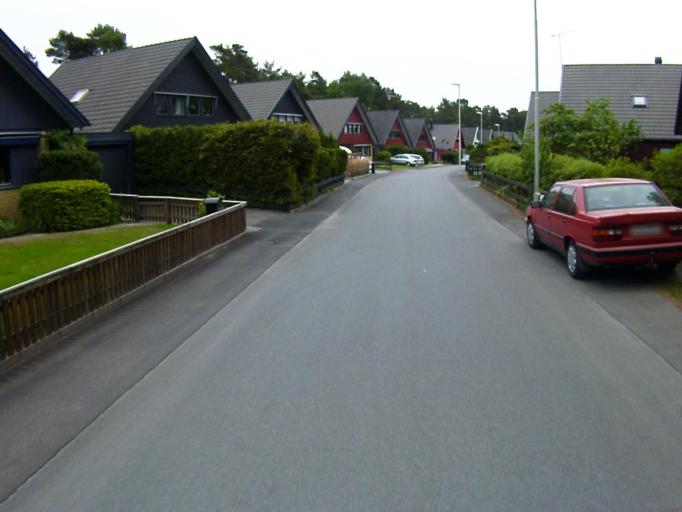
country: SE
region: Skane
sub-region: Kristianstads Kommun
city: Ahus
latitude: 55.9091
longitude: 14.2750
